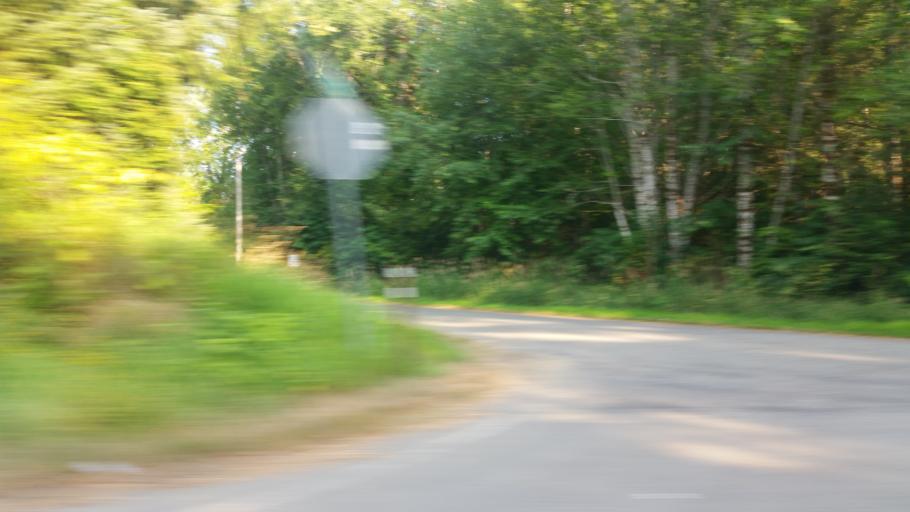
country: US
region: Washington
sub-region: Clallam County
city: Forks
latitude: 47.9069
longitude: -124.5390
